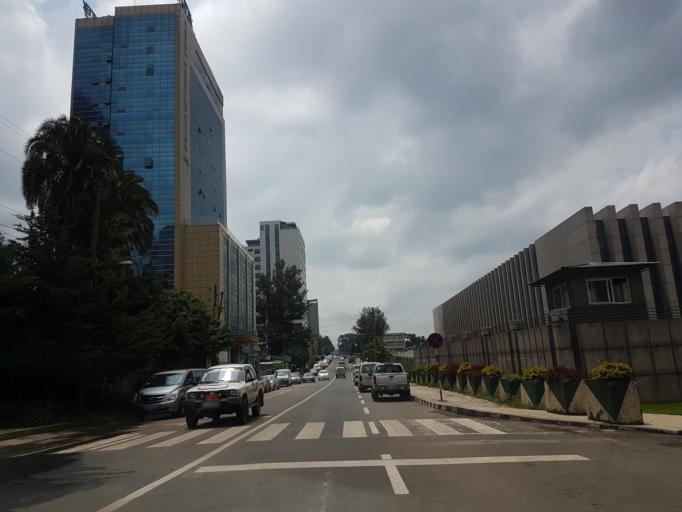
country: ET
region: Adis Abeba
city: Addis Ababa
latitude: 9.0024
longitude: 38.7432
